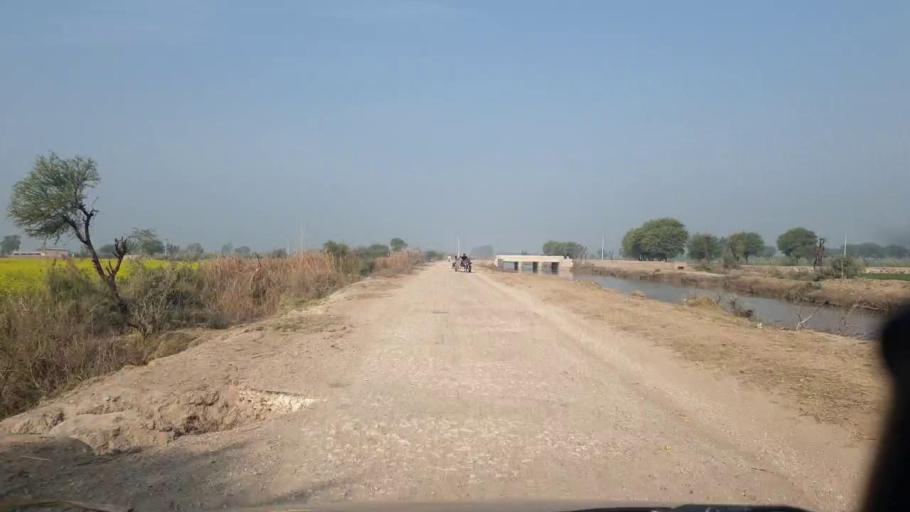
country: PK
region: Sindh
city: Shahdadpur
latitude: 26.0387
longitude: 68.5287
